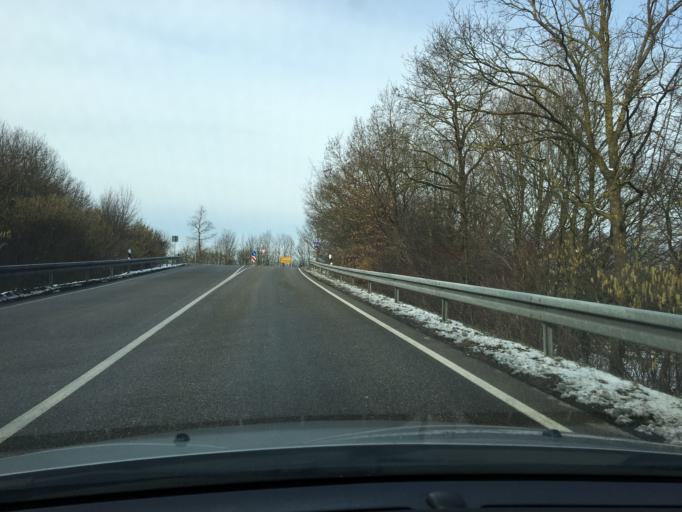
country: DE
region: Bavaria
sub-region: Upper Bavaria
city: Oberding
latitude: 48.3591
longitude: 11.8352
